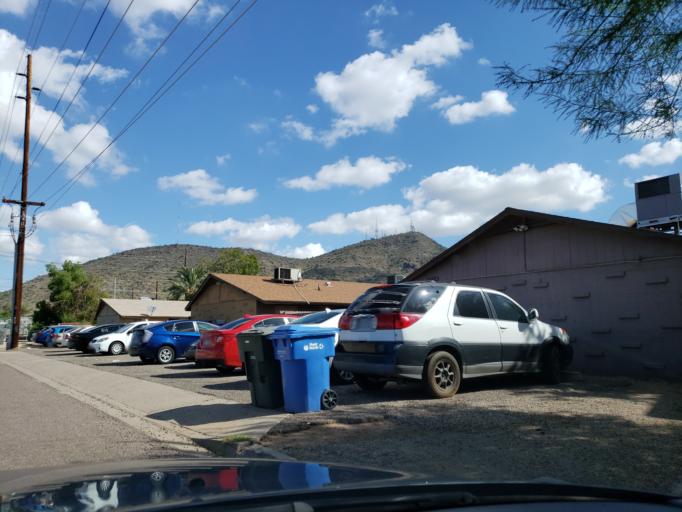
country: US
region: Arizona
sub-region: Maricopa County
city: Glendale
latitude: 33.5848
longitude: -112.0976
